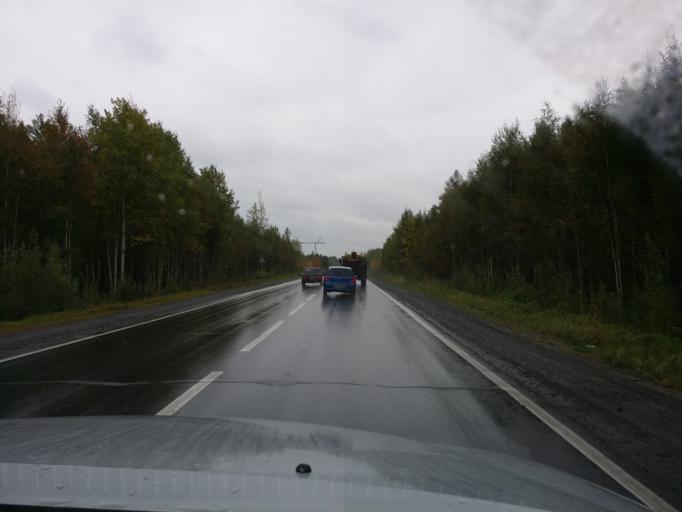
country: RU
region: Khanty-Mansiyskiy Avtonomnyy Okrug
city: Megion
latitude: 61.1612
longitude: 75.7121
